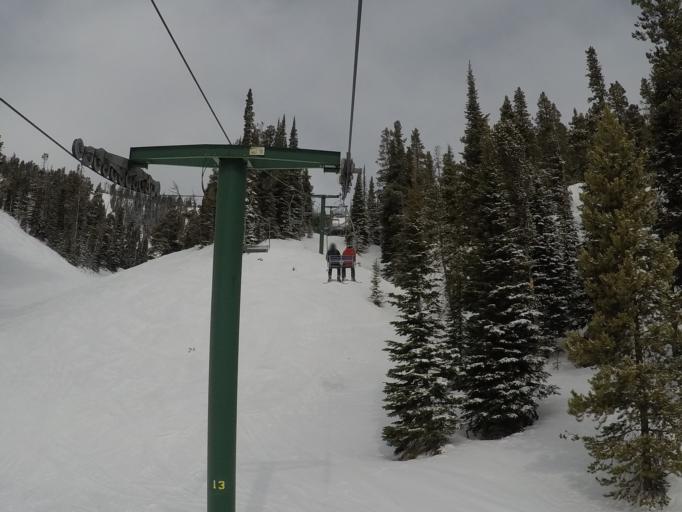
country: US
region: Montana
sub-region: Meagher County
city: White Sulphur Springs
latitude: 46.8331
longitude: -110.7087
